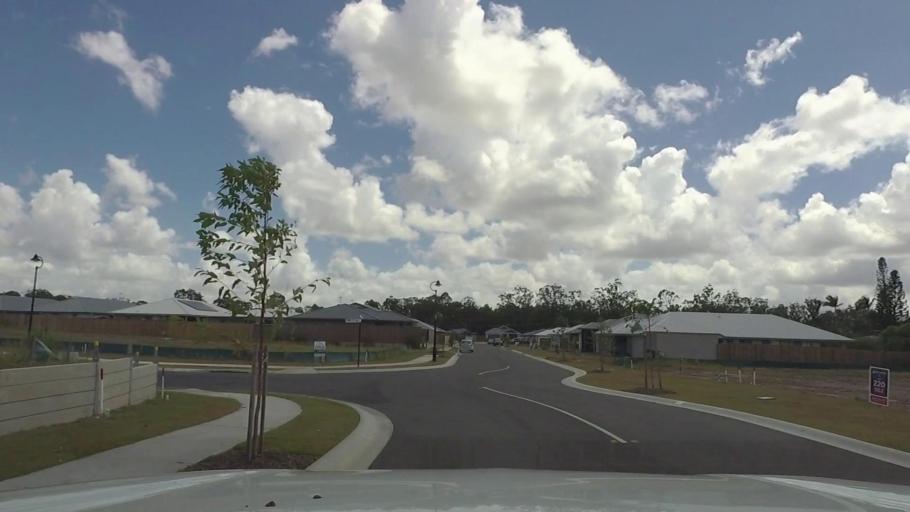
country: AU
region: Queensland
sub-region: Logan
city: Logan Reserve
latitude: -27.7090
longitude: 153.0805
